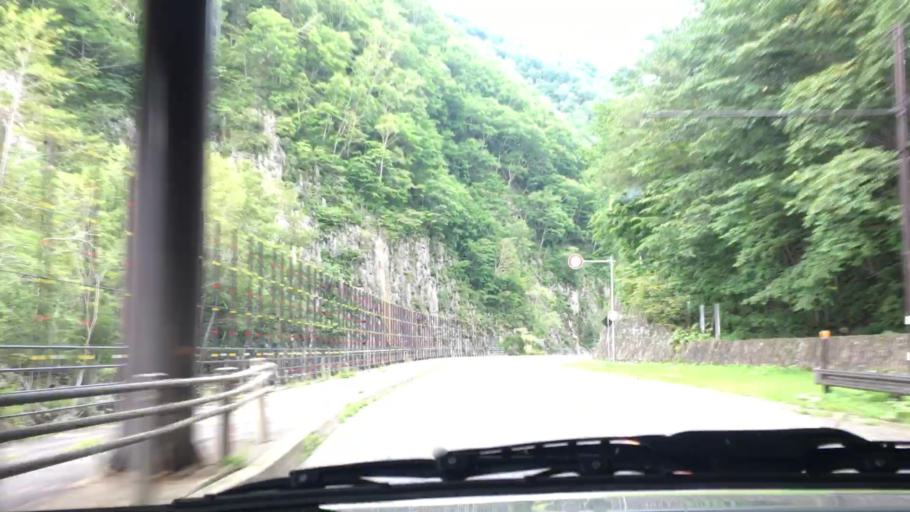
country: JP
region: Hokkaido
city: Otofuke
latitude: 43.3623
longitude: 143.2411
